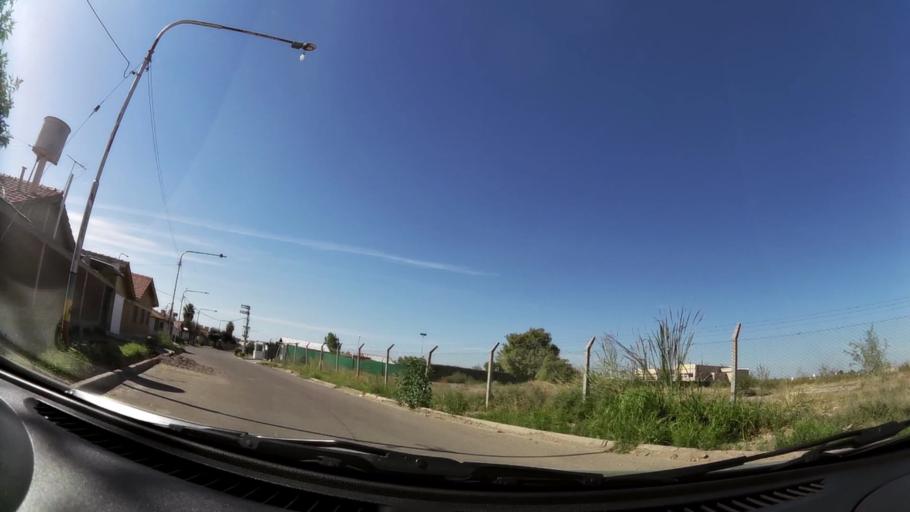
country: AR
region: Mendoza
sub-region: Departamento de Godoy Cruz
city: Godoy Cruz
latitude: -32.9507
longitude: -68.8134
